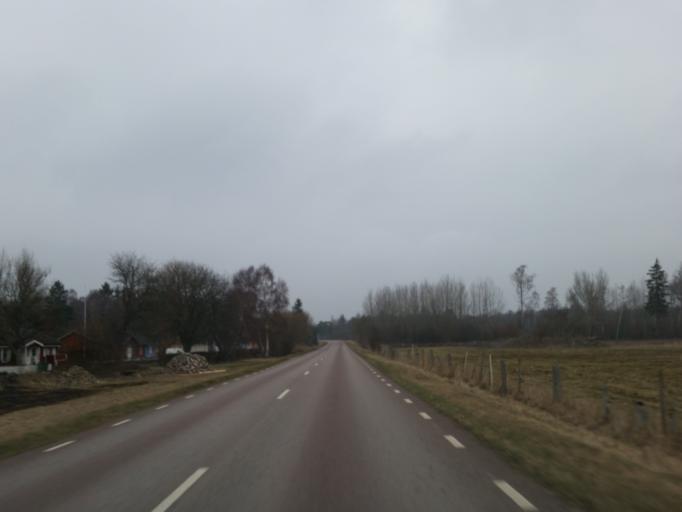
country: SE
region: Kalmar
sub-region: Morbylanga Kommun
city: Sodra Sandby
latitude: 56.6185
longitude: 16.6073
